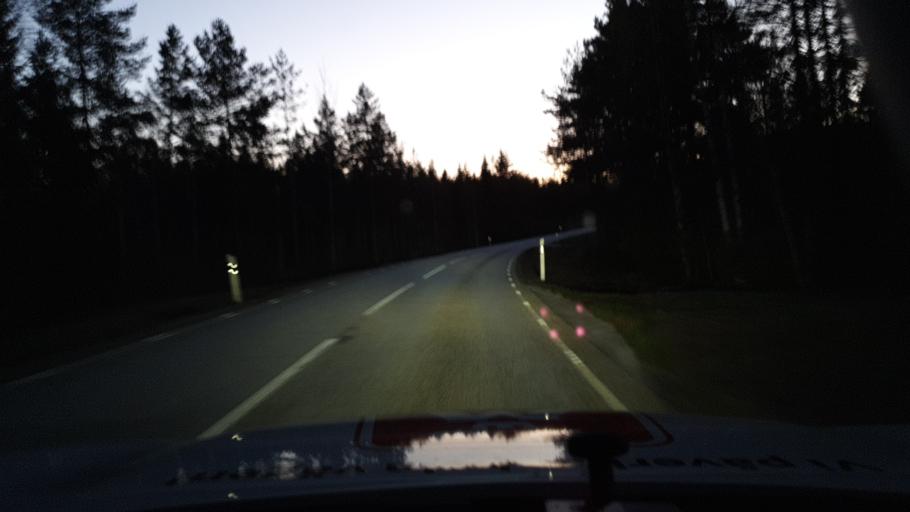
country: SE
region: OErebro
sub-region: Hallefors Kommun
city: Haellefors
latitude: 59.8071
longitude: 14.6970
